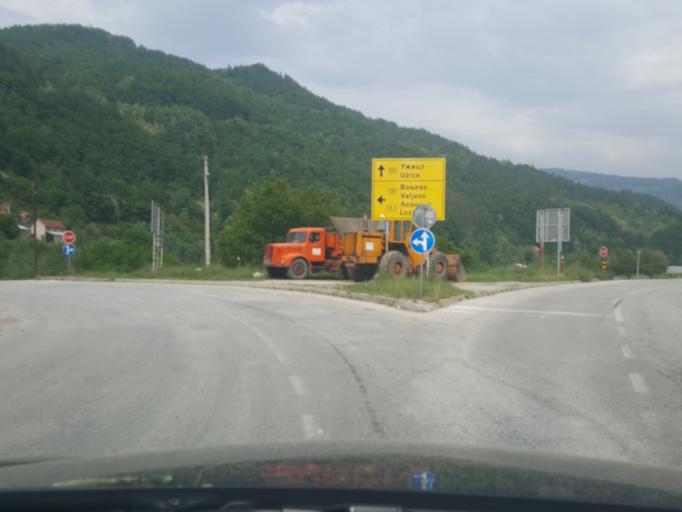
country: RS
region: Central Serbia
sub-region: Zlatiborski Okrug
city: Bajina Basta
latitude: 44.0405
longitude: 19.6250
